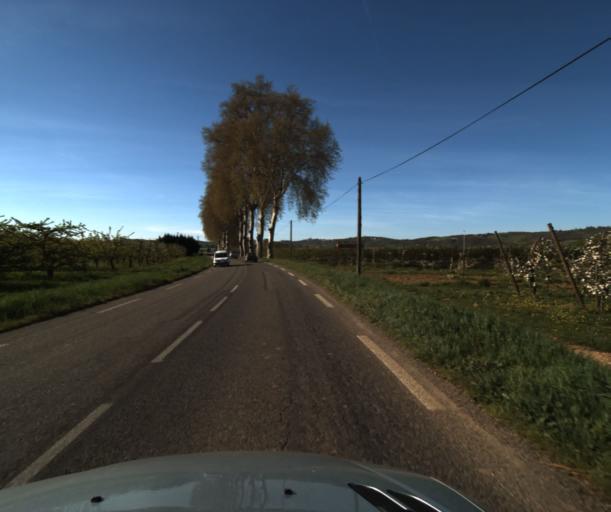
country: FR
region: Midi-Pyrenees
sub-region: Departement du Tarn-et-Garonne
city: Lafrancaise
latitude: 44.0922
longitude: 1.2648
